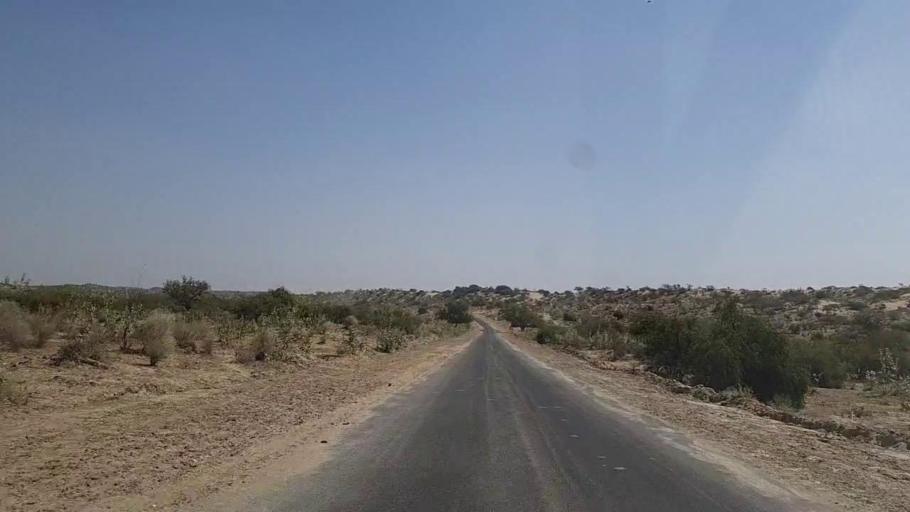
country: PK
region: Sindh
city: Diplo
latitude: 24.4816
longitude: 69.4822
